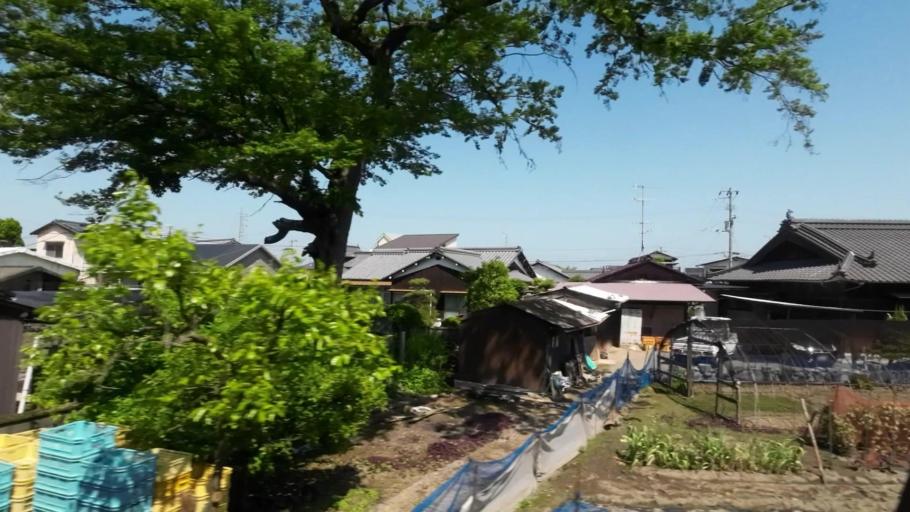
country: JP
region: Ehime
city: Niihama
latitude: 33.9596
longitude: 133.3079
